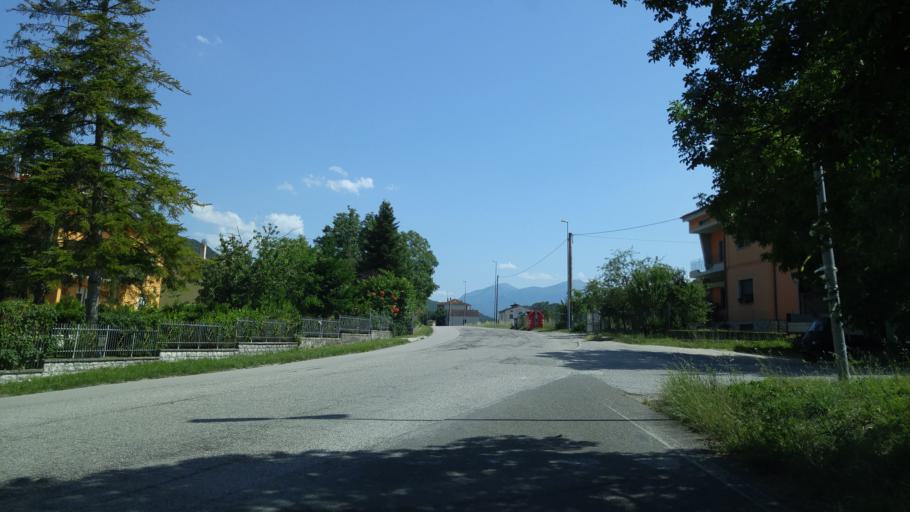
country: IT
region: The Marches
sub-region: Provincia di Pesaro e Urbino
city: Acqualagna
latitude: 43.6136
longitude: 12.6719
